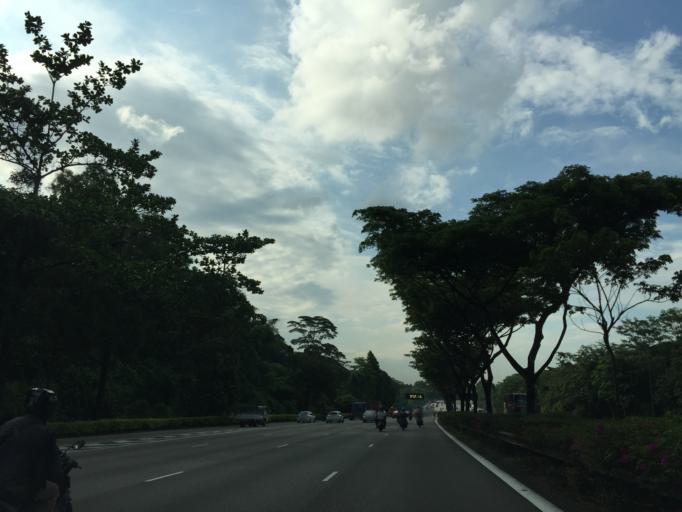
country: MY
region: Johor
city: Johor Bahru
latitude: 1.4116
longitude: 103.7714
